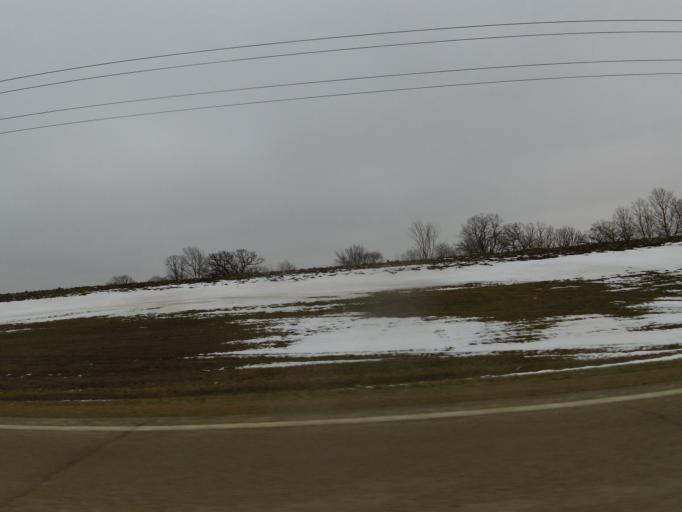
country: US
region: Minnesota
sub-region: Carver County
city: Carver
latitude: 44.7420
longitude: -93.6842
